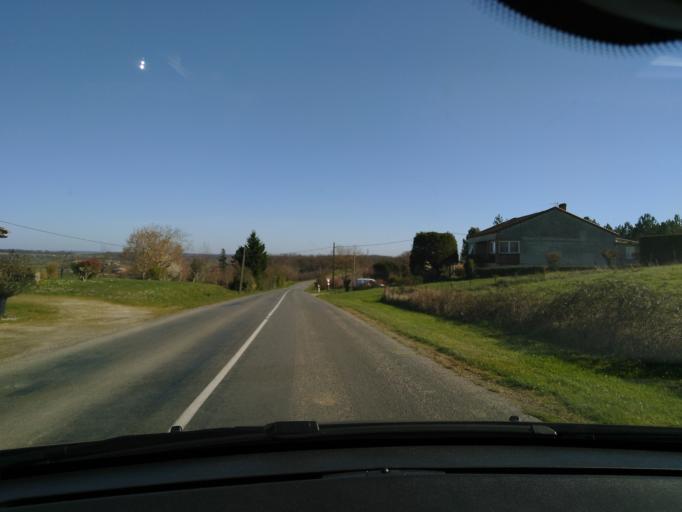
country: FR
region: Aquitaine
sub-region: Departement du Lot-et-Garonne
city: Cancon
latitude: 44.5350
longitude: 0.6369
